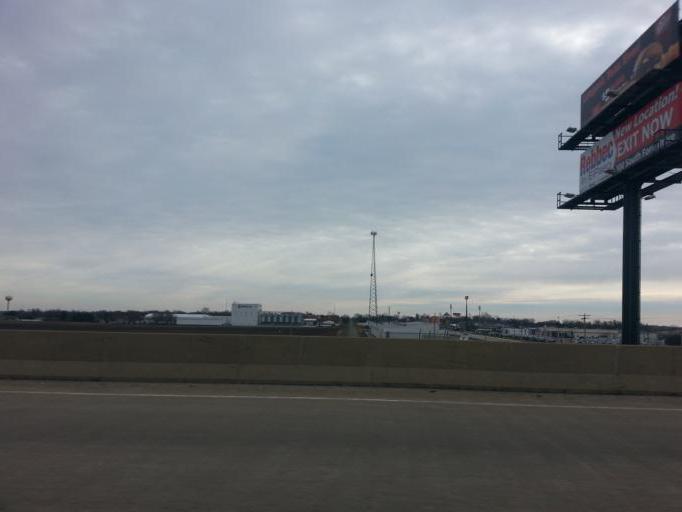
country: US
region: Illinois
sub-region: Woodford County
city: El Paso
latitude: 40.7375
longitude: -89.0343
